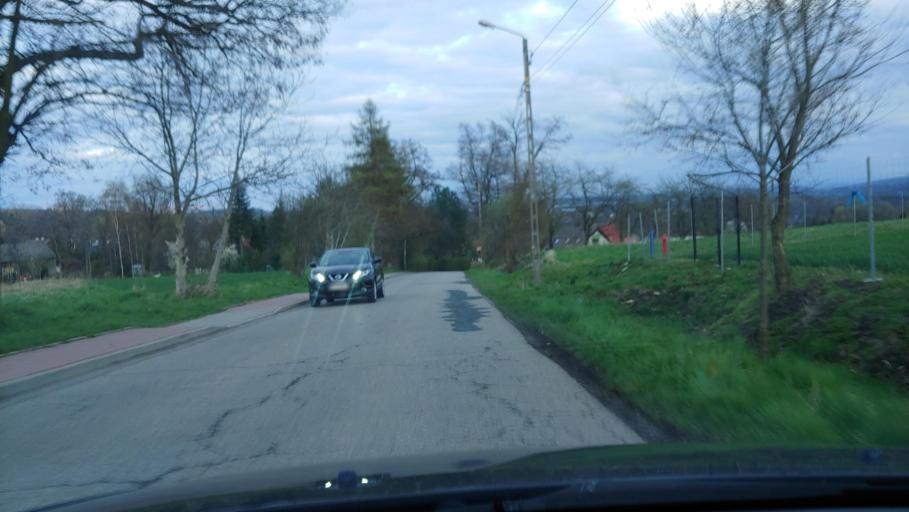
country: PL
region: Lesser Poland Voivodeship
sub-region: Powiat krakowski
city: Bolechowice
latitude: 50.1483
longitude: 19.7849
